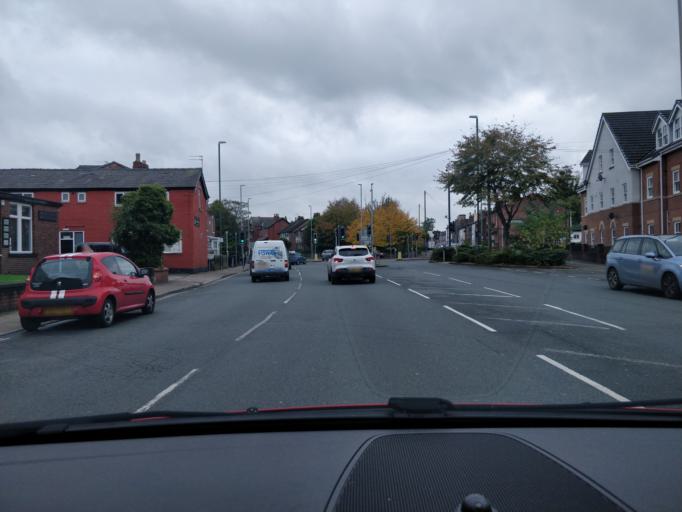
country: GB
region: England
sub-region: Lancashire
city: Ormskirk
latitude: 53.5664
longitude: -2.8832
